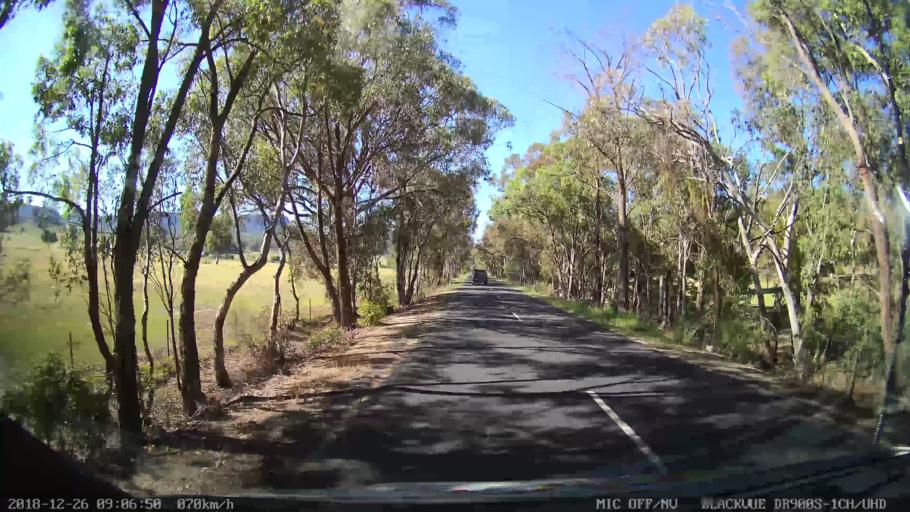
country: AU
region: New South Wales
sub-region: Mid-Western Regional
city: Kandos
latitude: -32.6989
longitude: 150.0056
